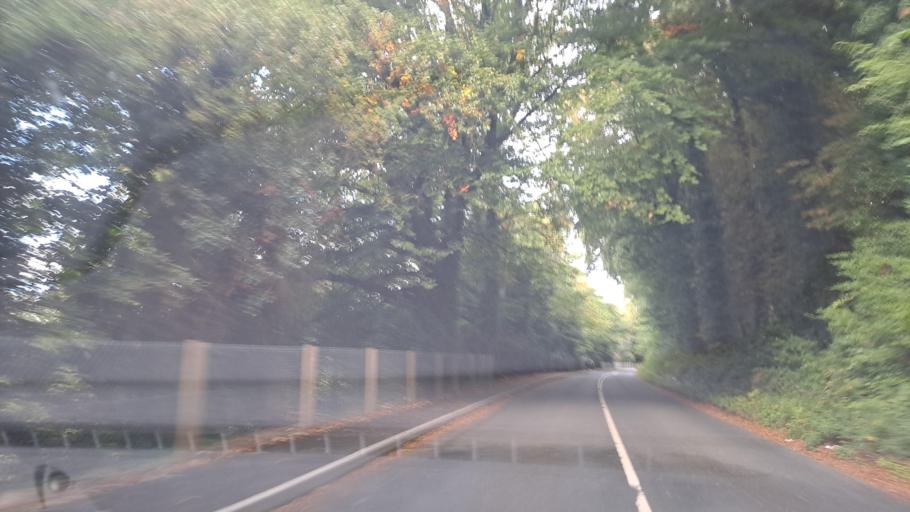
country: IE
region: Ulster
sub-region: County Monaghan
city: Carrickmacross
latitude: 53.9655
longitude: -6.6942
